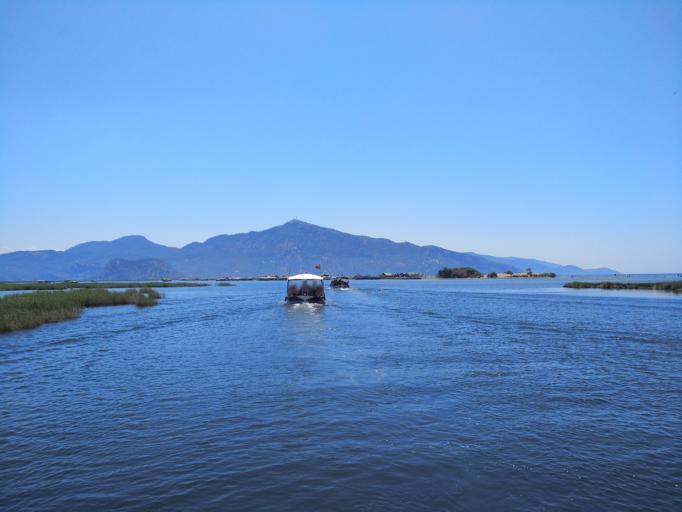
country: TR
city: Dalyan
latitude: 36.8052
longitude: 28.6038
